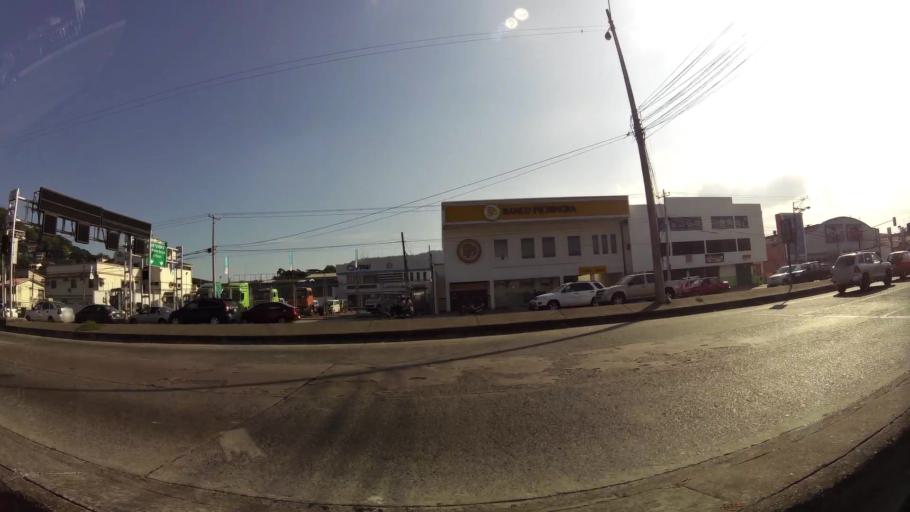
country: EC
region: Guayas
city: Guayaquil
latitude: -2.1594
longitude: -79.9283
